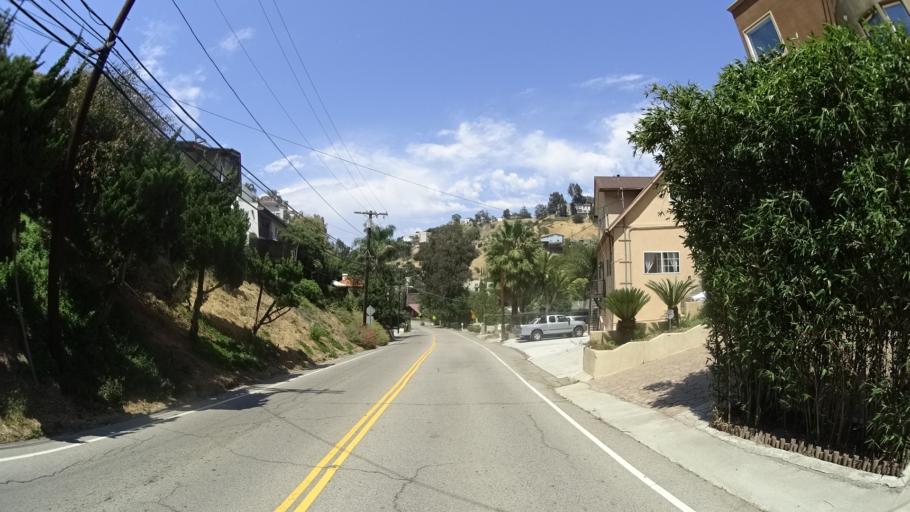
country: US
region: California
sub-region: Los Angeles County
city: Sherman Oaks
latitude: 34.1352
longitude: -118.4135
